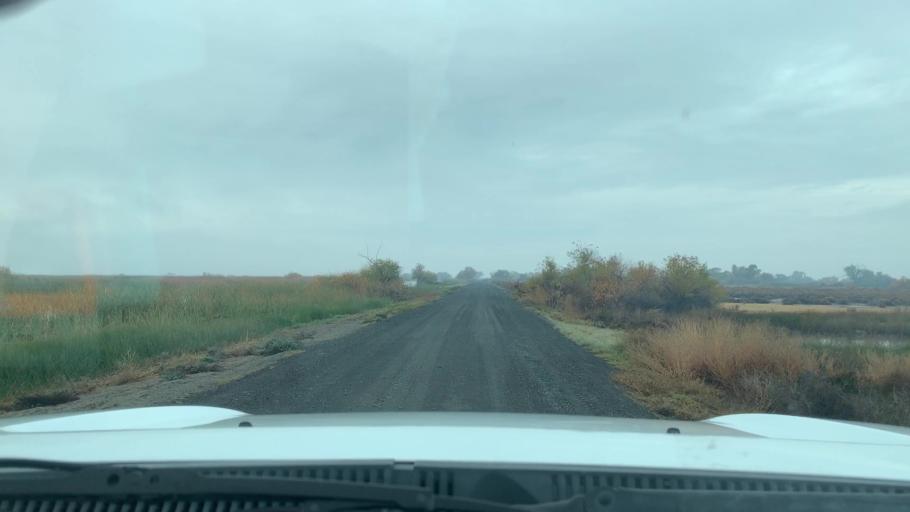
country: US
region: California
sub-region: Kern County
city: Lost Hills
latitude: 35.7336
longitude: -119.5910
